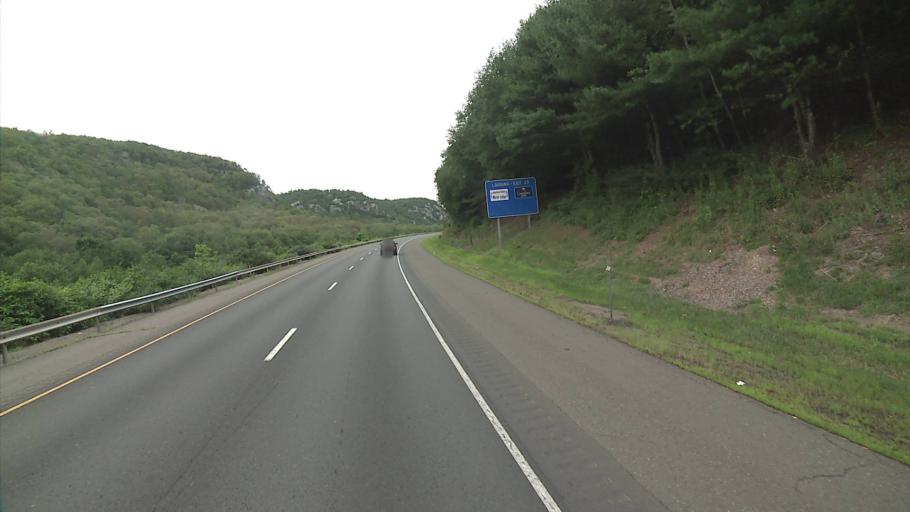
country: US
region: Connecticut
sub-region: New Haven County
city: Naugatuck
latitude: 41.4499
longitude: -73.0663
